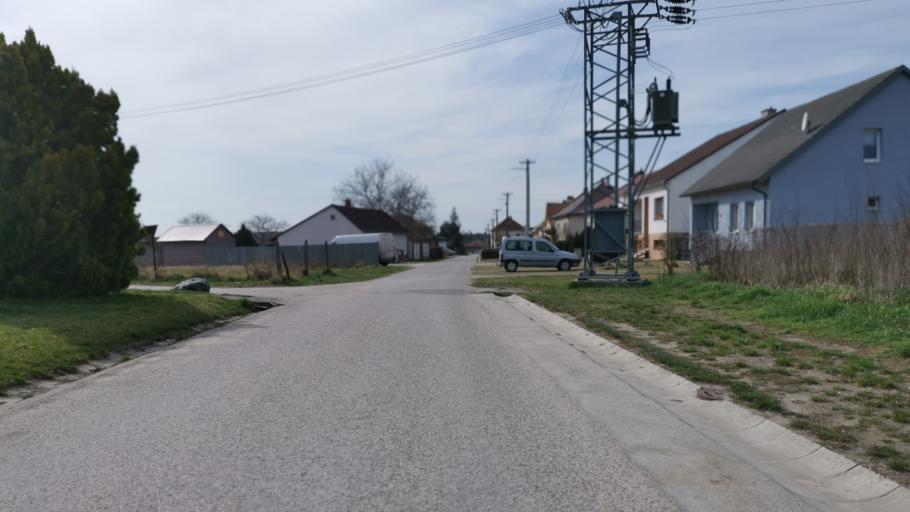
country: SK
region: Trnavsky
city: Gbely
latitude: 48.6572
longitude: 17.0851
